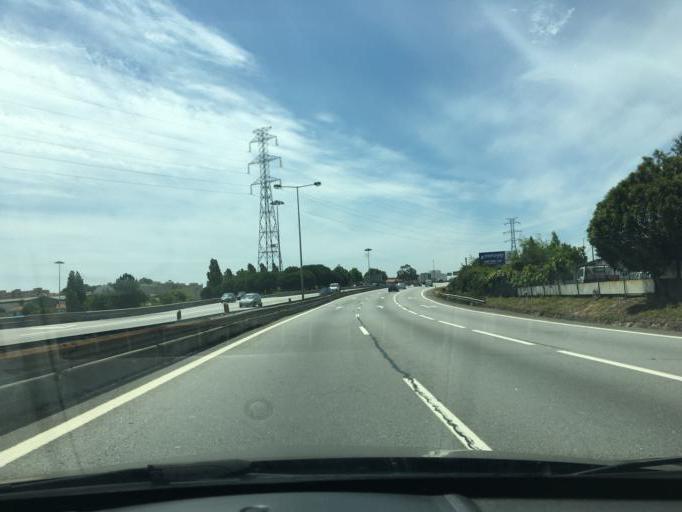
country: PT
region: Porto
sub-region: Matosinhos
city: Sao Mamede de Infesta
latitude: 41.1832
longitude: -8.6227
